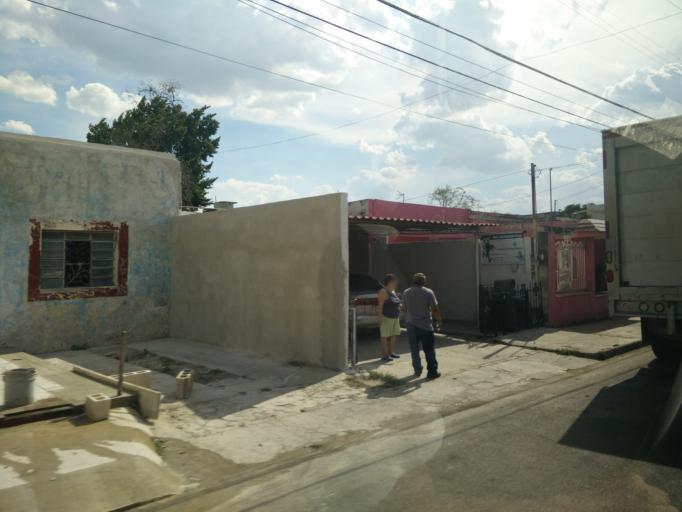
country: MX
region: Yucatan
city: Merida
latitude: 20.9644
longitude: -89.5926
